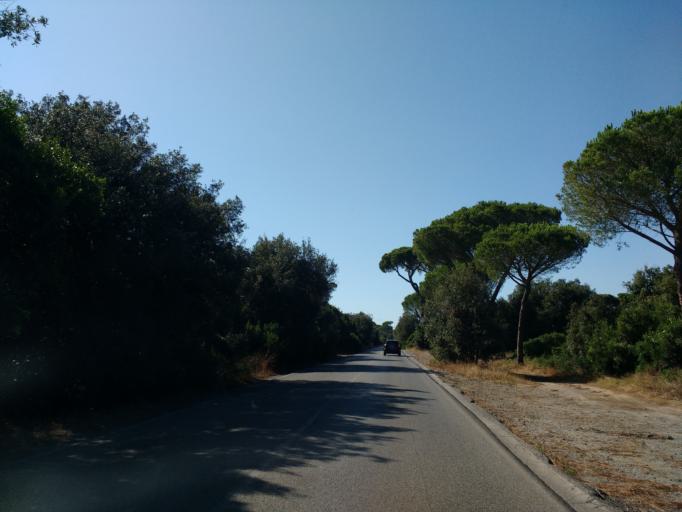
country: IT
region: Latium
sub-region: Citta metropolitana di Roma Capitale
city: Acilia-Castel Fusano-Ostia Antica
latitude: 41.7164
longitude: 12.3530
